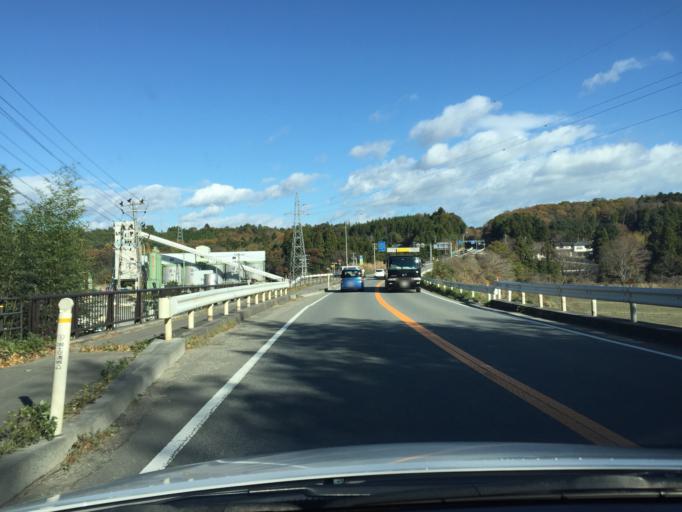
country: JP
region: Fukushima
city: Namie
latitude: 37.2876
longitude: 140.9911
